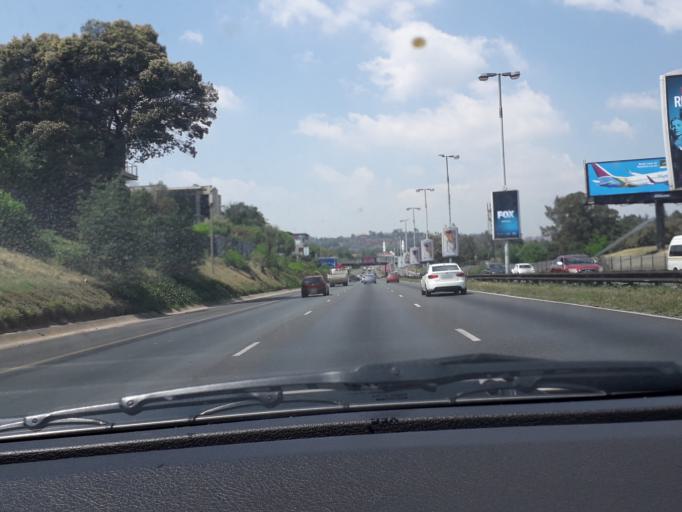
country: ZA
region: Gauteng
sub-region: City of Johannesburg Metropolitan Municipality
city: Johannesburg
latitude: -26.1529
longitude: 28.0573
